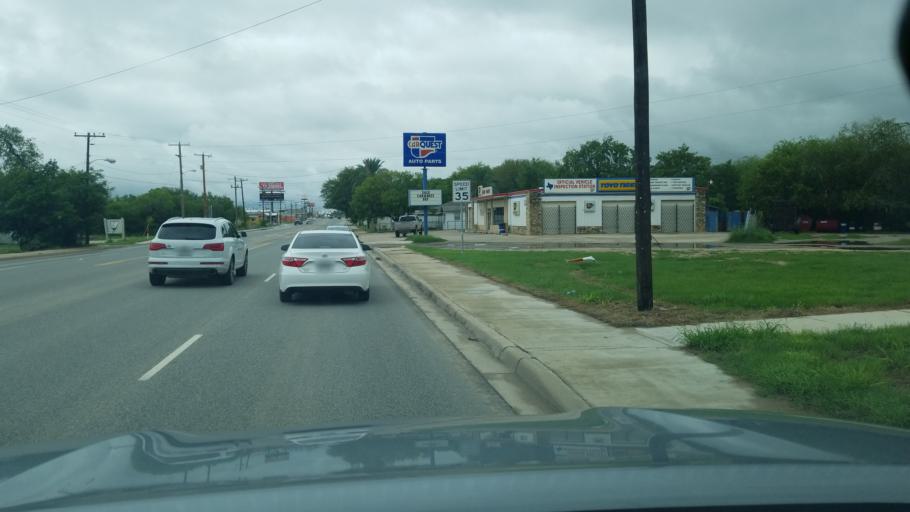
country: US
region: Texas
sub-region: Dimmit County
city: Carrizo Springs
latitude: 28.5277
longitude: -99.8546
